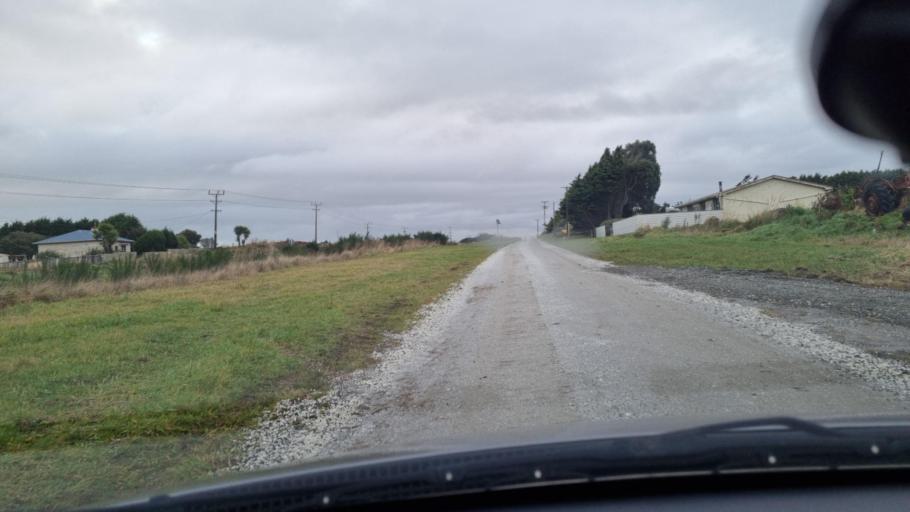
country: NZ
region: Southland
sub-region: Invercargill City
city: Bluff
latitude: -46.5463
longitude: 168.3015
